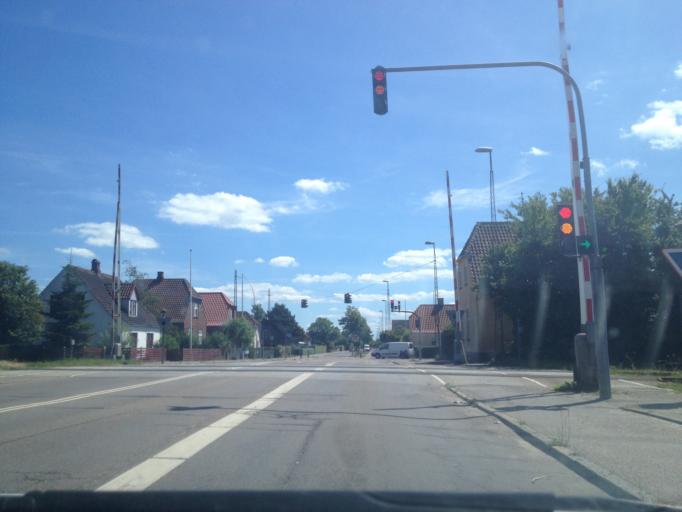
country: DK
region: Zealand
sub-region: Kalundborg Kommune
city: Kalundborg
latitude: 55.6776
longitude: 11.1060
